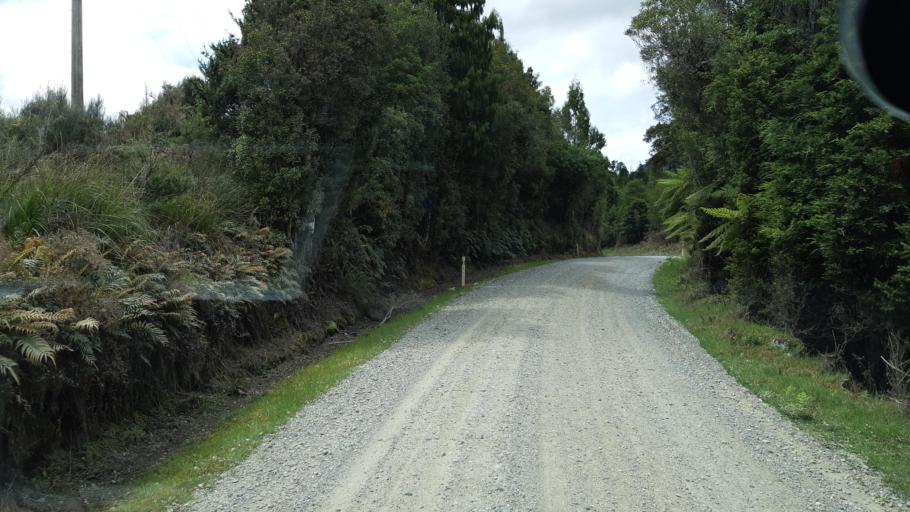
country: NZ
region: West Coast
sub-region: Westland District
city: Hokitika
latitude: -42.7292
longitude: 171.2305
